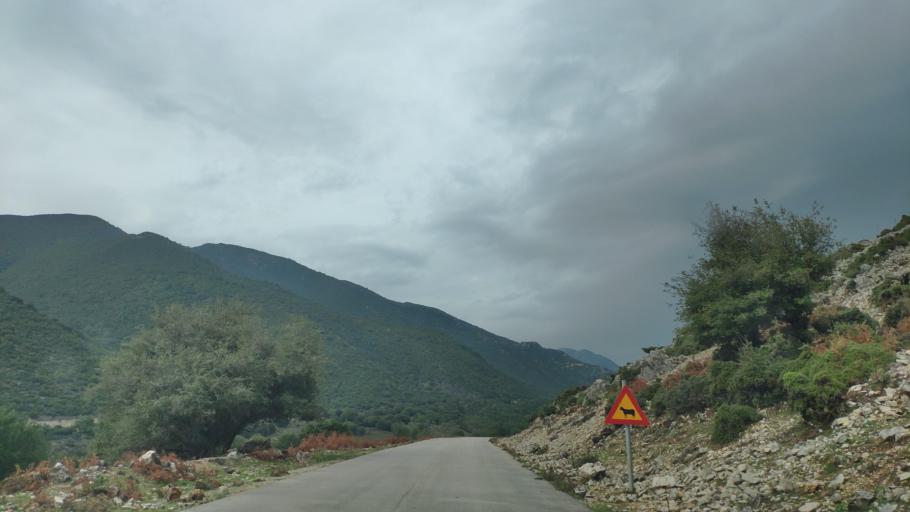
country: GR
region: Epirus
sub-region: Nomos Thesprotias
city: Paramythia
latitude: 39.3854
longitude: 20.6250
